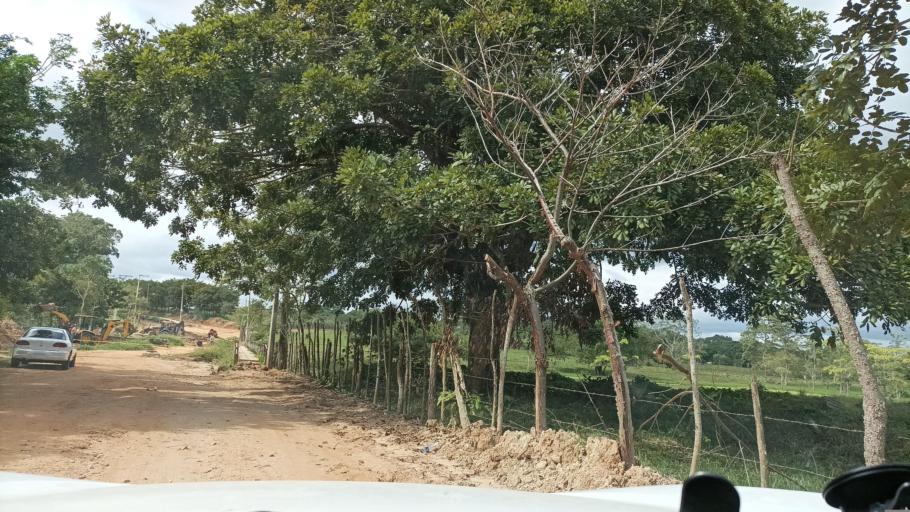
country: MX
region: Veracruz
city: Soconusco
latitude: 17.9668
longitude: -94.8872
